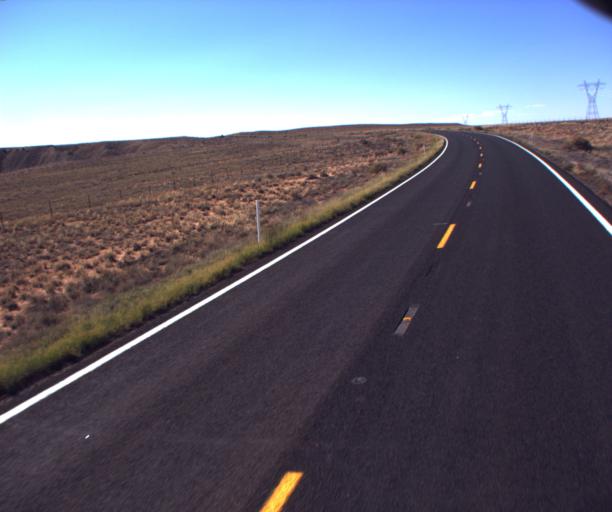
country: US
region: Arizona
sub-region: Coconino County
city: Tuba City
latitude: 35.9717
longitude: -110.8380
